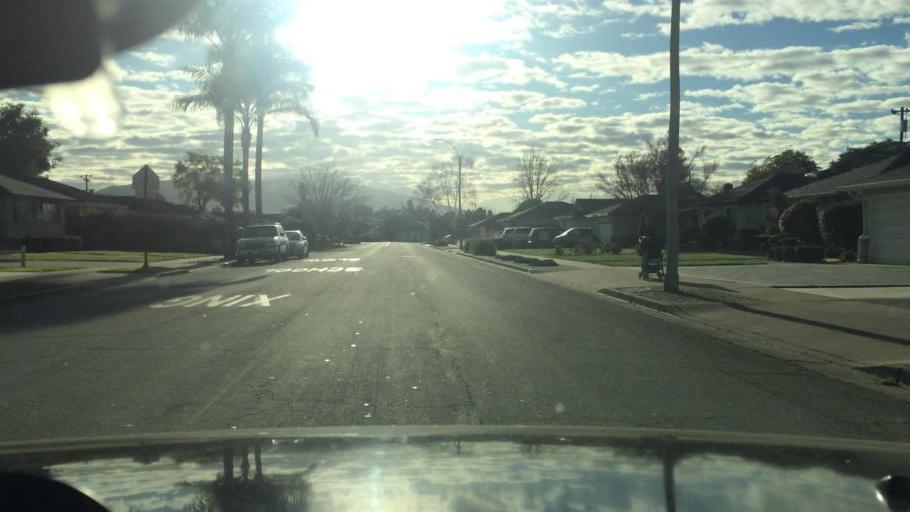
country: US
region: California
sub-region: Alameda County
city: Fremont
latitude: 37.5480
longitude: -121.9964
